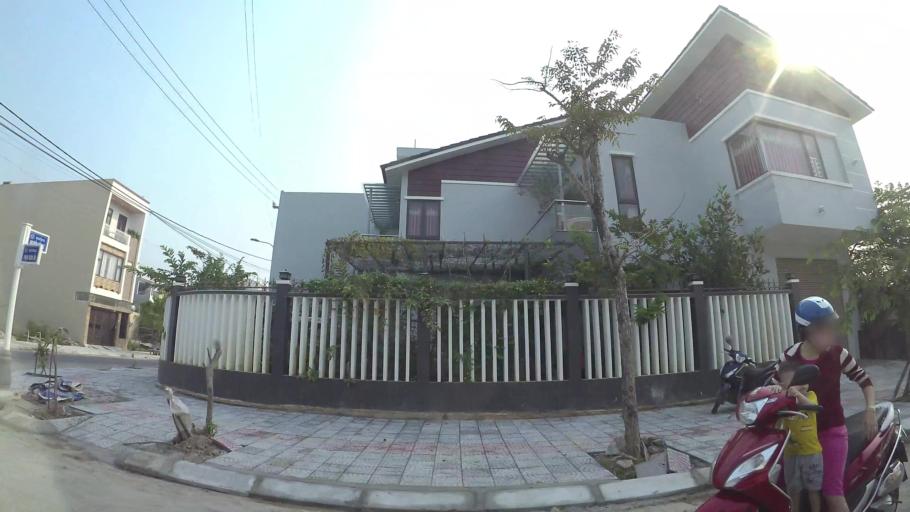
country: VN
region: Da Nang
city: Cam Le
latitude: 16.0089
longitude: 108.2230
